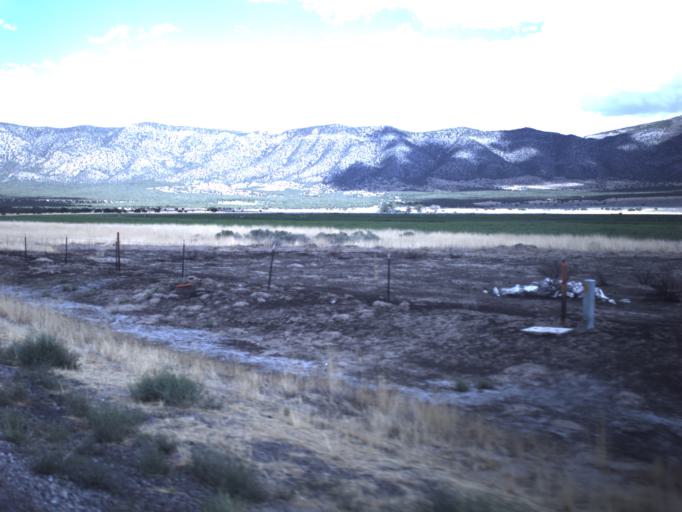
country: US
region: Utah
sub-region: Tooele County
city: Grantsville
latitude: 40.3003
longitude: -112.6491
